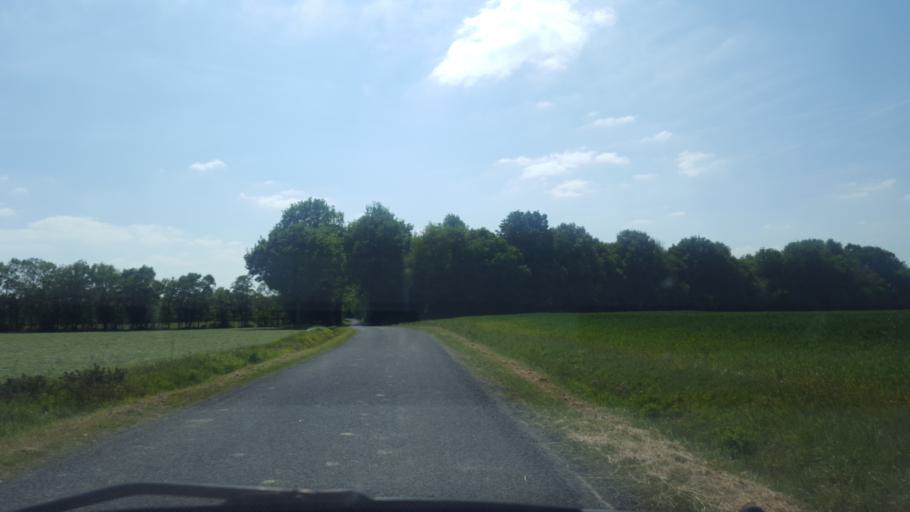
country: FR
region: Pays de la Loire
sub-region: Departement de la Loire-Atlantique
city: Saint-Philbert-de-Grand-Lieu
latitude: 47.0301
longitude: -1.6139
